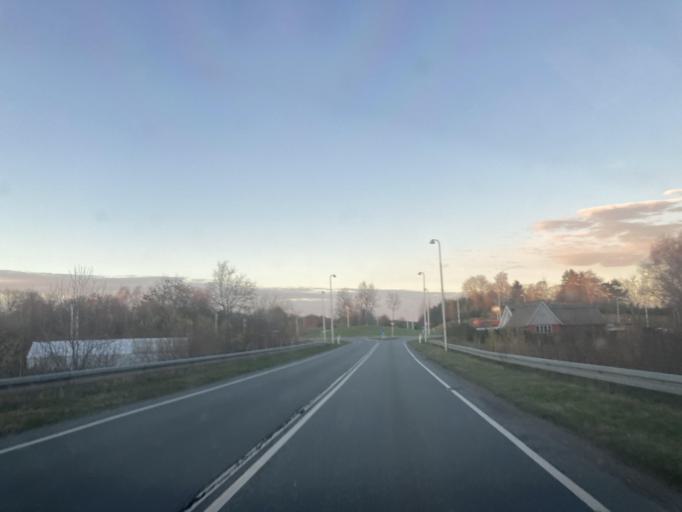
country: DK
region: Capital Region
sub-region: Gribskov Kommune
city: Graested
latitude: 56.0594
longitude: 12.2742
